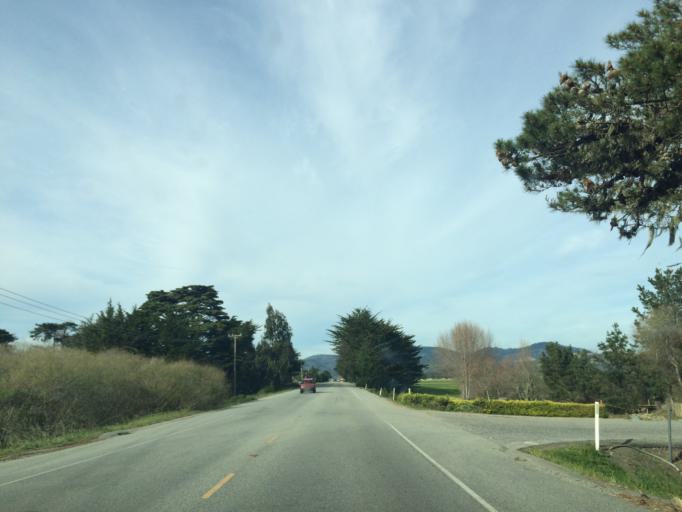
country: US
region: California
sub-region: San Mateo County
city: Half Moon Bay
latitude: 37.4397
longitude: -122.4277
